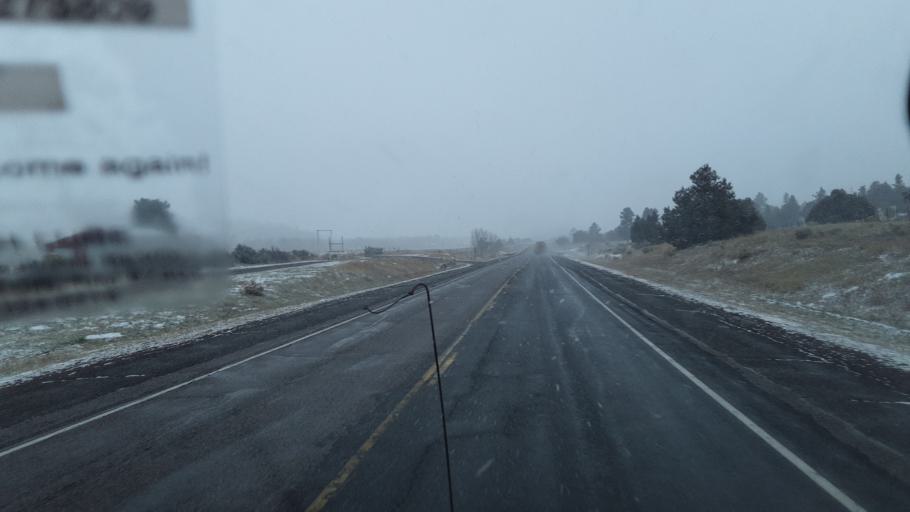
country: US
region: New Mexico
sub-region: Rio Arriba County
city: Chama
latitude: 36.8162
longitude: -106.5687
